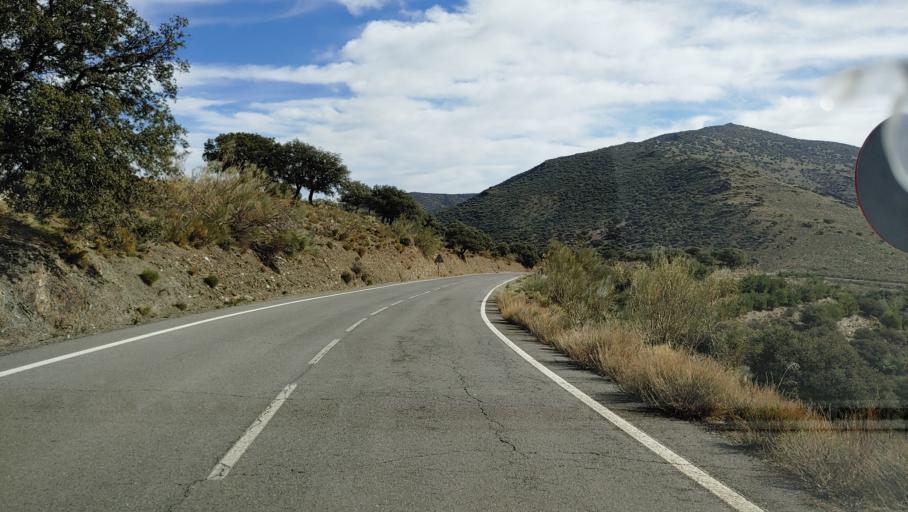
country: ES
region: Andalusia
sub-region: Provincia de Almeria
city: Ohanes
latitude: 37.0861
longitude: -2.7400
